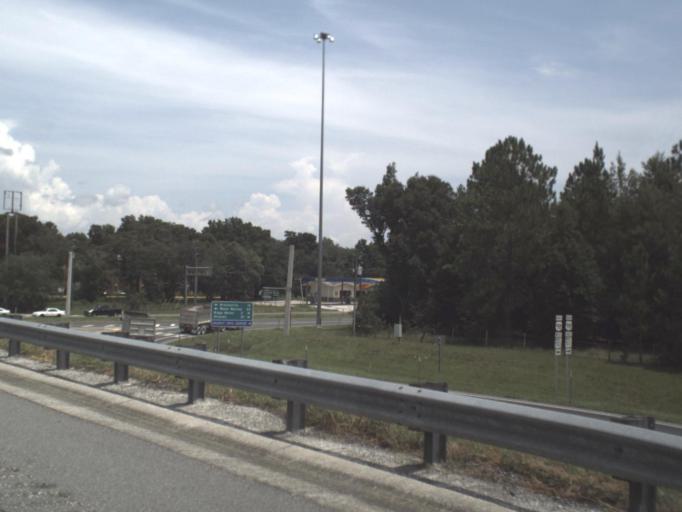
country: US
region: Florida
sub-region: Hernando County
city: Hill 'n Dale
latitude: 28.5220
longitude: -82.2369
